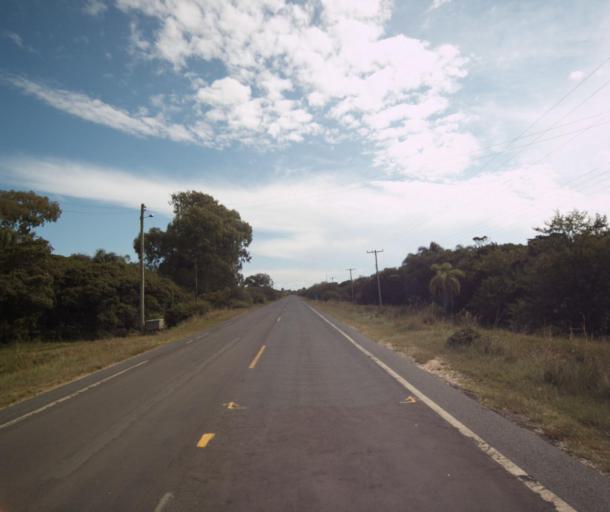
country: BR
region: Rio Grande do Sul
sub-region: Sao Lourenco Do Sul
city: Sao Lourenco do Sul
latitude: -31.6223
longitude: -51.4076
